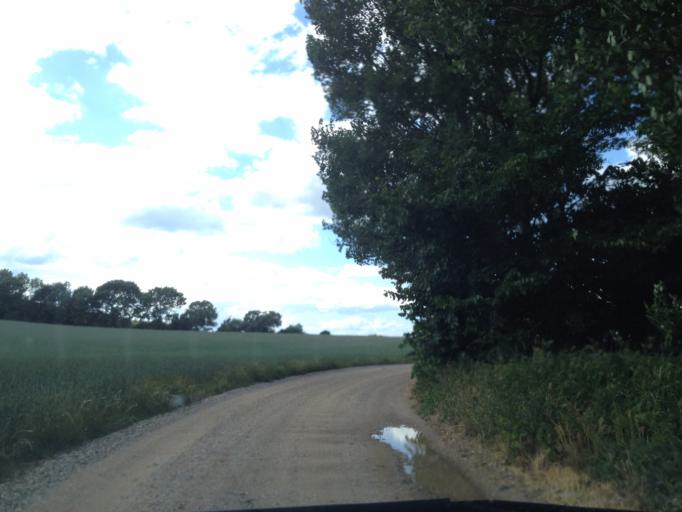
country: DK
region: Central Jutland
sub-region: Syddjurs Kommune
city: Ronde
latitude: 56.1995
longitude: 10.4841
